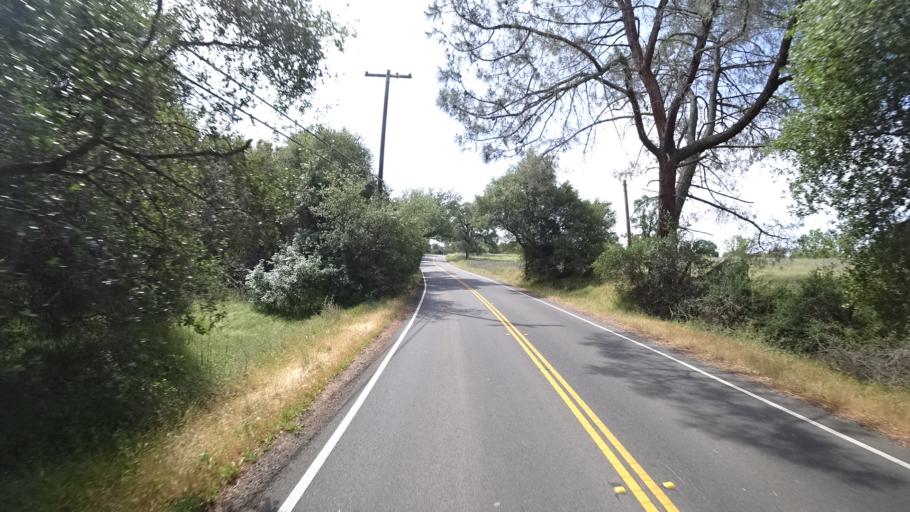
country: US
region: California
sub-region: Placer County
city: Loomis
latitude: 38.7948
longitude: -121.1924
